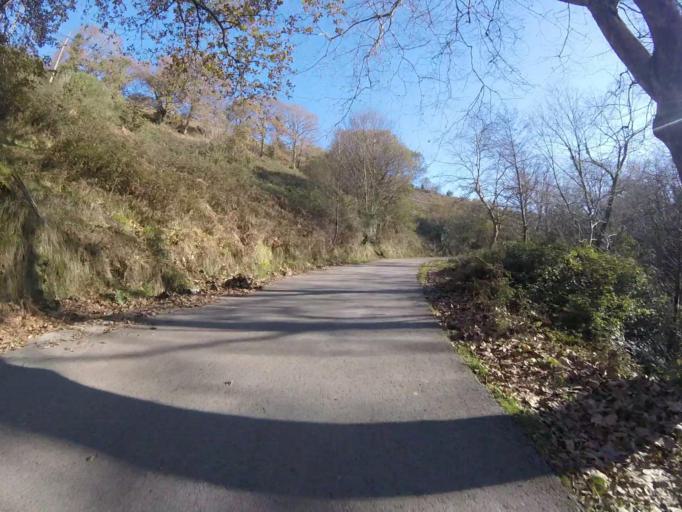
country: ES
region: Navarre
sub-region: Provincia de Navarra
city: Bera
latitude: 43.3084
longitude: -1.6824
